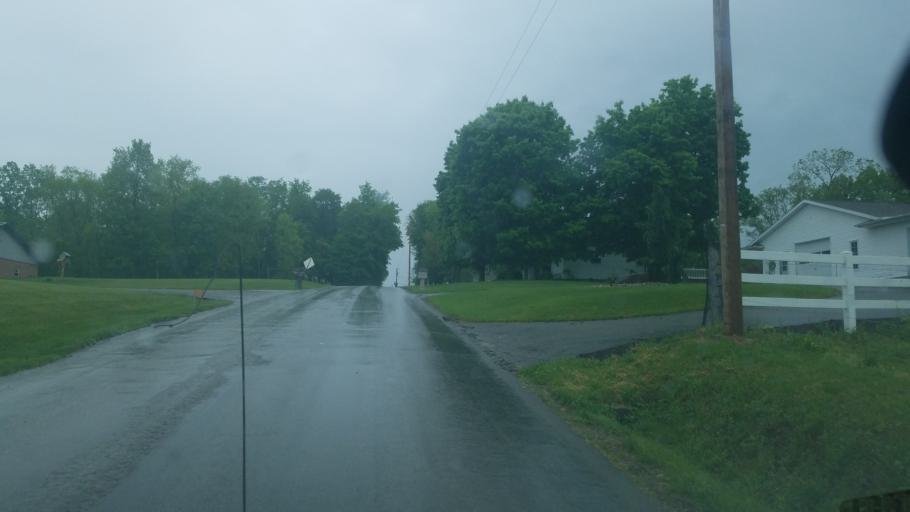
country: US
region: Ohio
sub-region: Wayne County
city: Apple Creek
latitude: 40.6944
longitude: -81.8424
